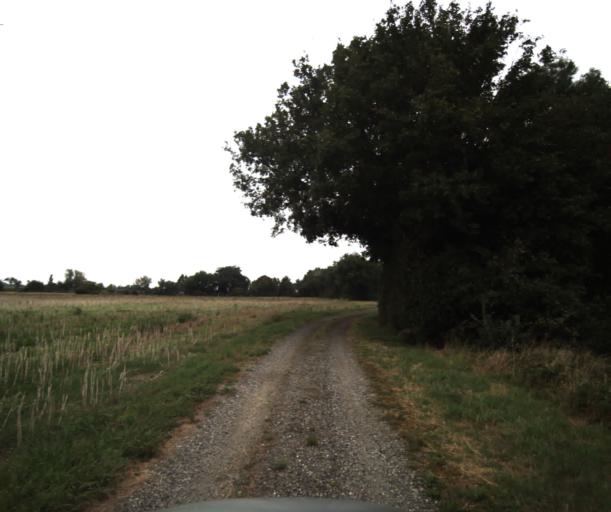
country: FR
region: Midi-Pyrenees
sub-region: Departement de la Haute-Garonne
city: Seysses
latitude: 43.4494
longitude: 1.3036
